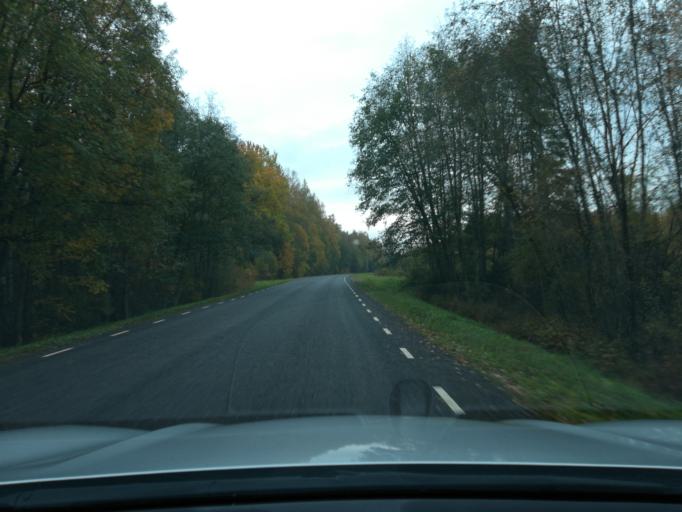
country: EE
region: Ida-Virumaa
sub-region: Johvi vald
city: Johvi
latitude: 59.0469
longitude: 27.3961
